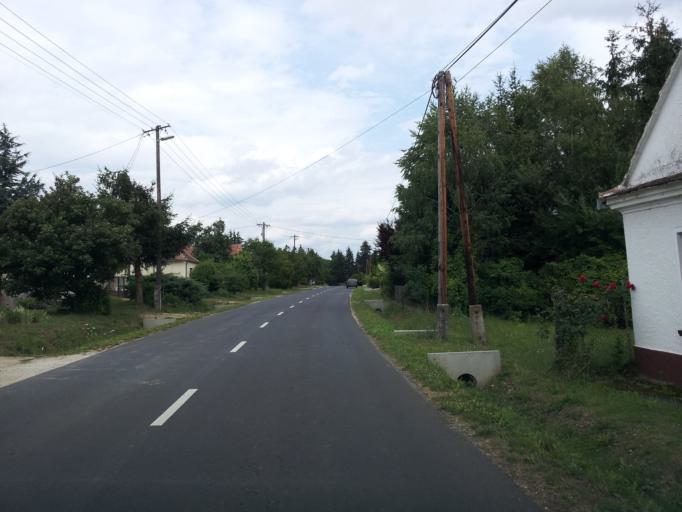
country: HU
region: Zala
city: Zalaszentgrot
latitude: 47.0330
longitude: 16.9763
